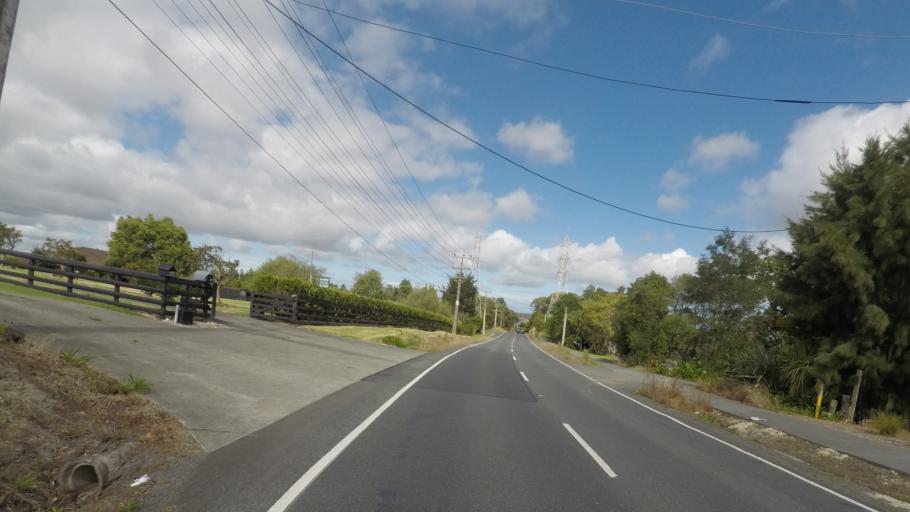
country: NZ
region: Auckland
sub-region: Auckland
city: Muriwai Beach
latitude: -36.7681
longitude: 174.5549
